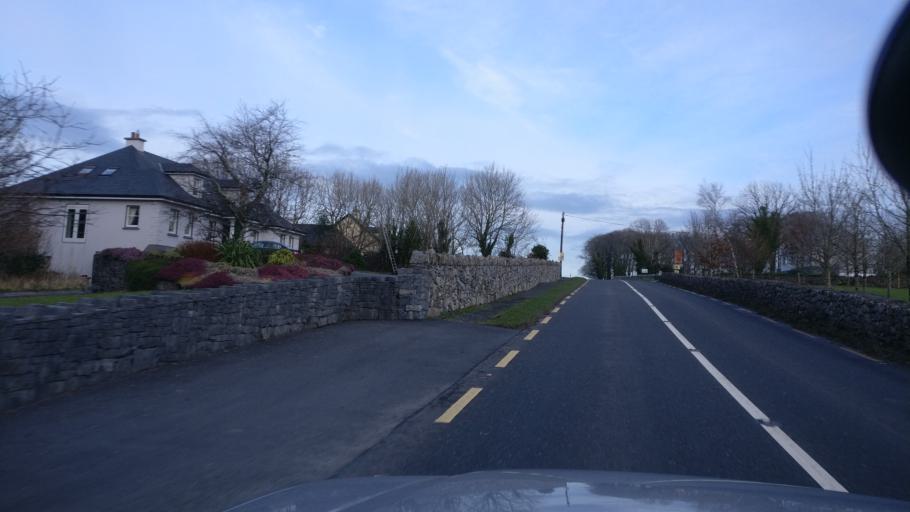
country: IE
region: Connaught
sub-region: Maigh Eo
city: Ballinrobe
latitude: 53.5407
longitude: -9.2602
